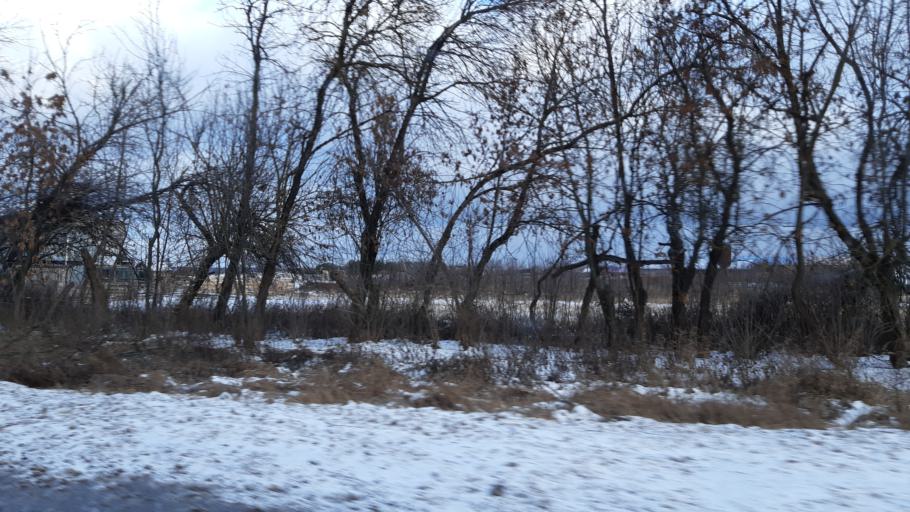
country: RU
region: Moskovskaya
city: Noginsk-9
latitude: 56.0162
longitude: 38.5577
